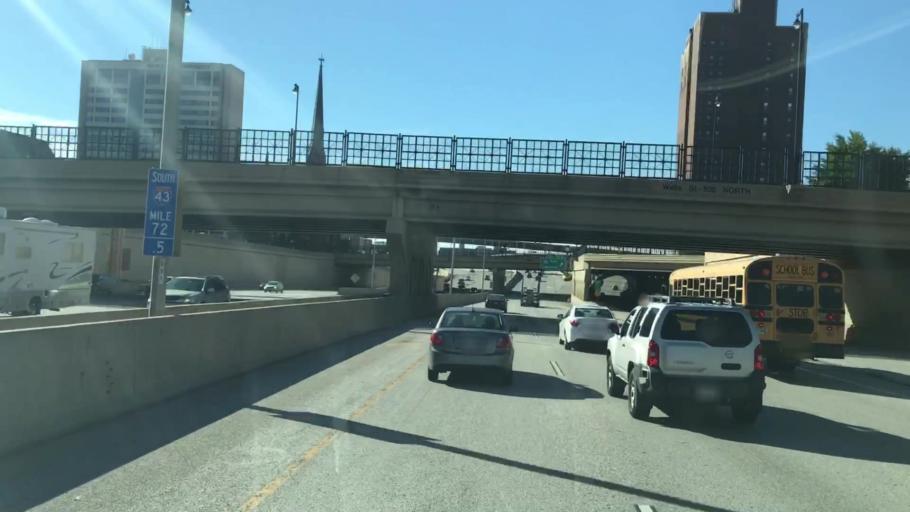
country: US
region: Wisconsin
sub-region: Milwaukee County
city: Milwaukee
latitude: 43.0407
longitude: -87.9252
